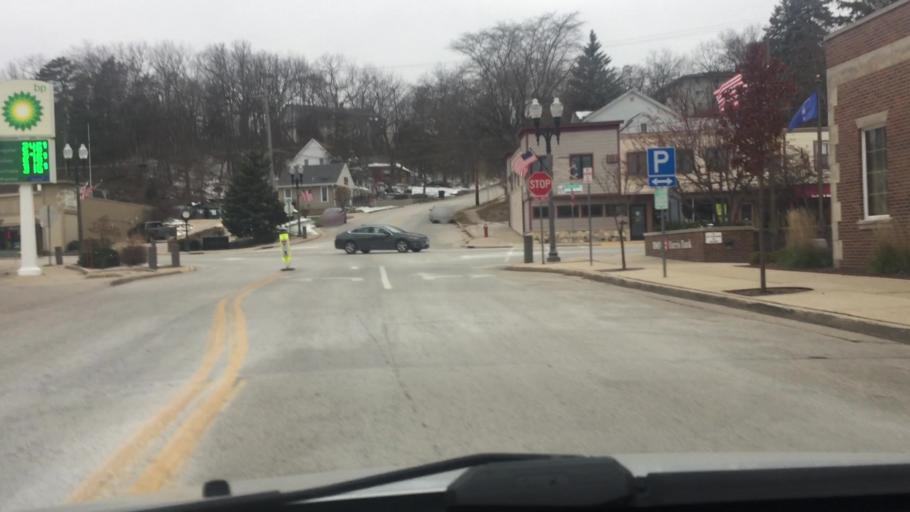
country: US
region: Wisconsin
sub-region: Waukesha County
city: Hartland
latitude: 43.1046
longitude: -88.3469
